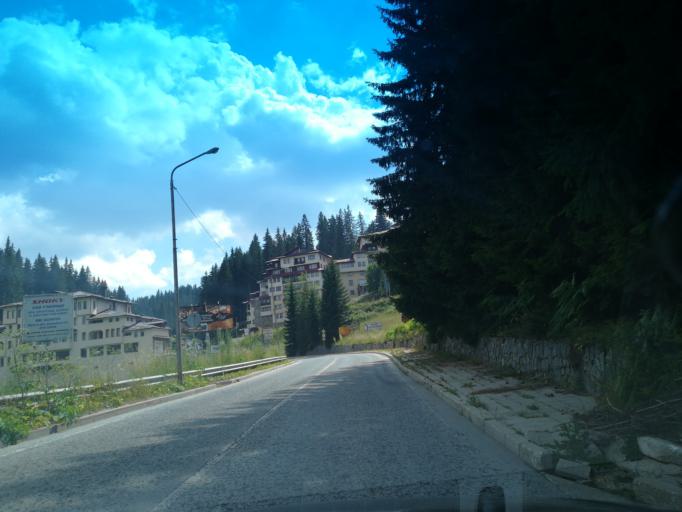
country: BG
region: Smolyan
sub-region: Obshtina Smolyan
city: Smolyan
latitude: 41.6519
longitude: 24.6956
